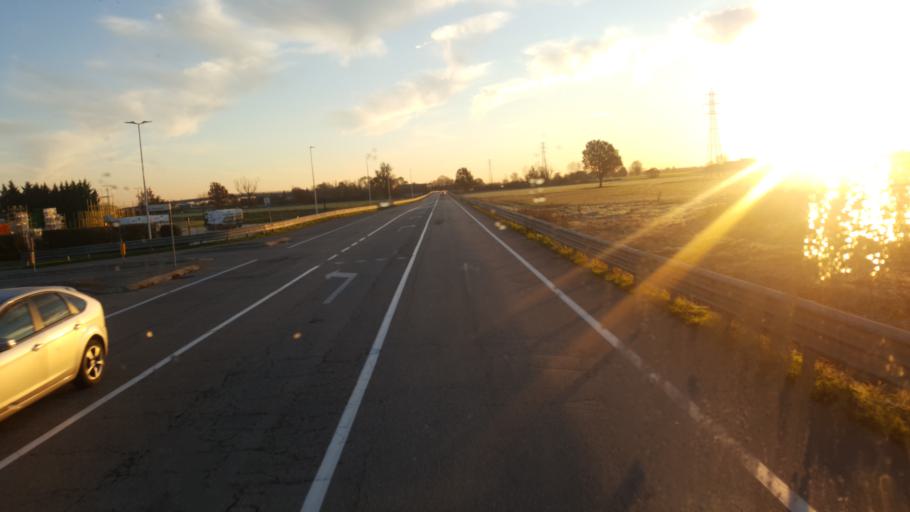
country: IT
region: Emilia-Romagna
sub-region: Provincia di Parma
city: Fontanellato
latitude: 44.8709
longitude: 10.1859
